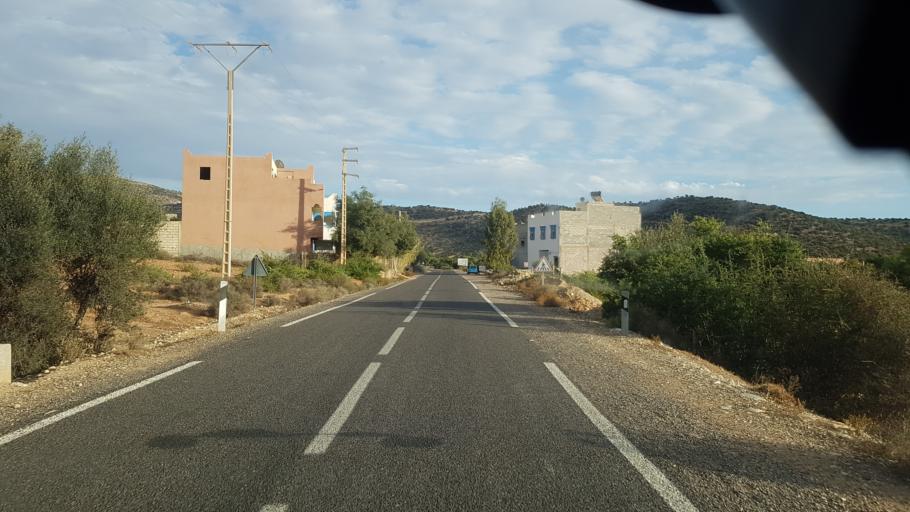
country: MA
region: Souss-Massa-Draa
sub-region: Agadir-Ida-ou-Tnan
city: Aourir
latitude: 30.5162
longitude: -9.5936
